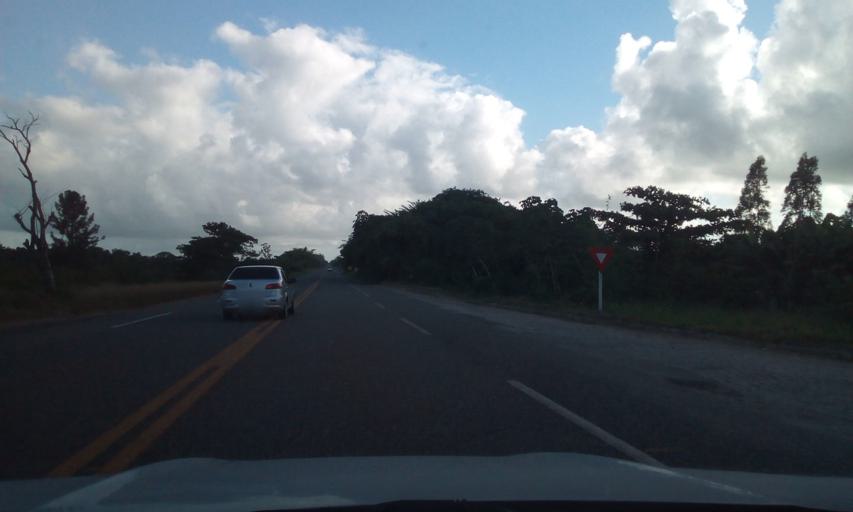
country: BR
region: Bahia
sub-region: Entre Rios
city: Entre Rios
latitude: -12.3010
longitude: -37.8996
